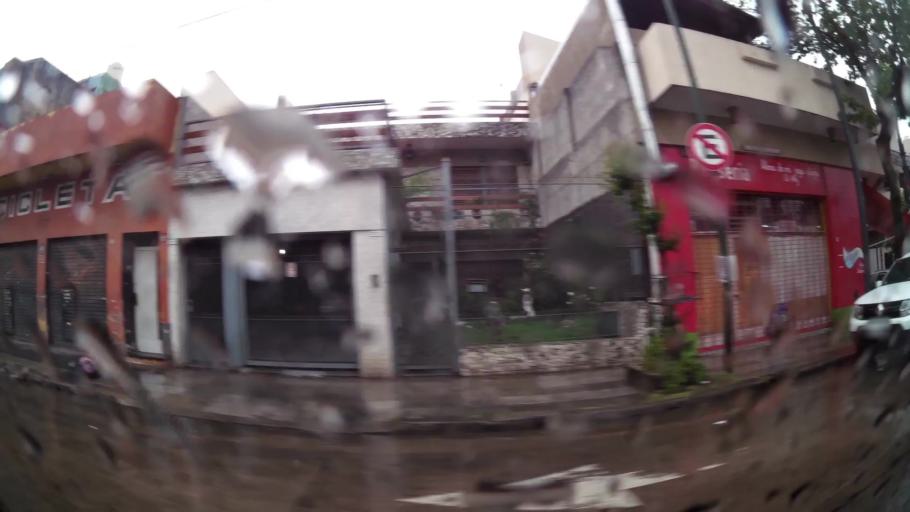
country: AR
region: Buenos Aires F.D.
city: Villa Lugano
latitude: -34.6603
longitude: -58.4438
